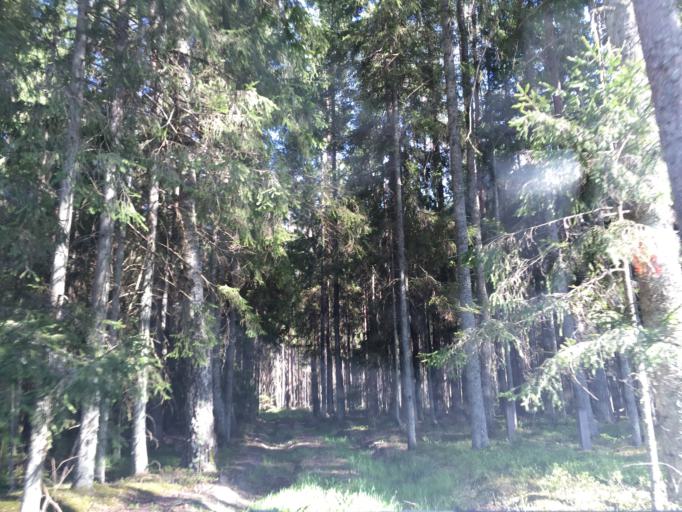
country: LV
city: Tireli
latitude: 56.8149
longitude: 23.6883
